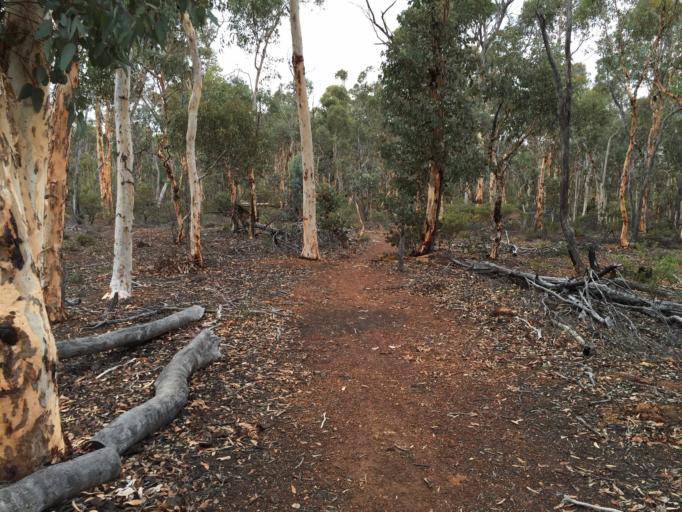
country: AU
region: Western Australia
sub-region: Narrogin
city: Narrogin
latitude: -32.7997
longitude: 116.9409
